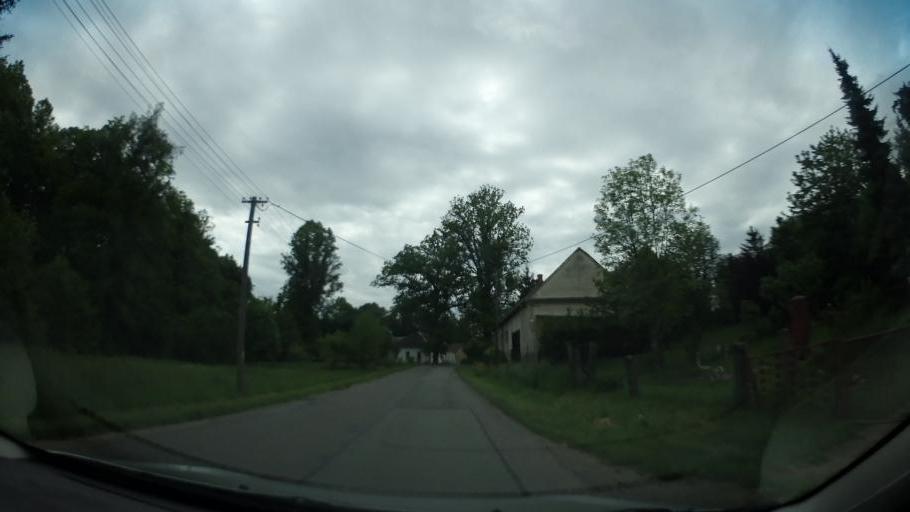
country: CZ
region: Pardubicky
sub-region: Okres Svitavy
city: Moravska Trebova
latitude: 49.8205
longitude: 16.7008
